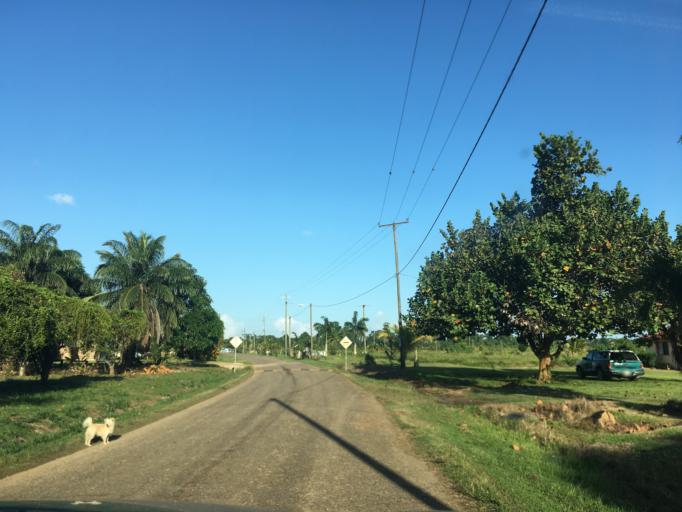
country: BZ
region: Stann Creek
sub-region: Dangriga
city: Dangriga
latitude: 16.8190
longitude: -88.3310
